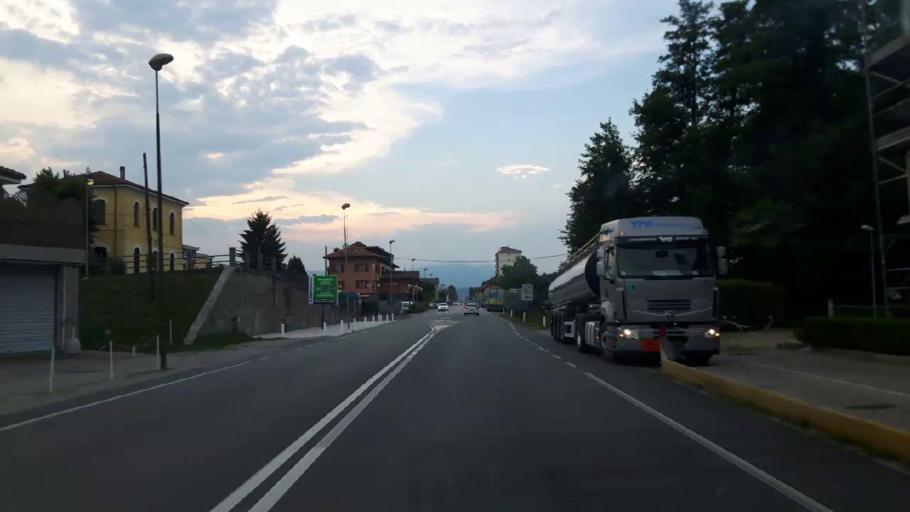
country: IT
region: Piedmont
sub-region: Provincia di Novara
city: Comignago
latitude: 45.7230
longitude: 8.5830
